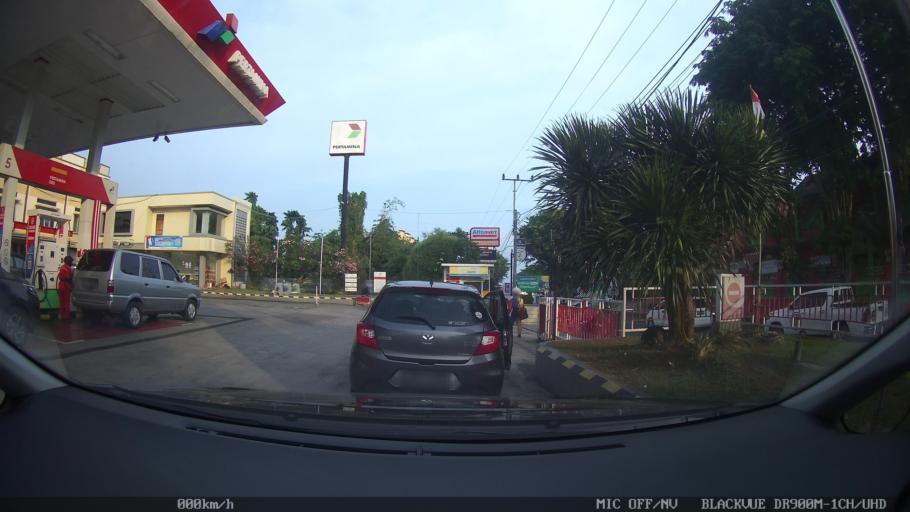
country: ID
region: Lampung
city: Bandarlampung
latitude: -5.4363
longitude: 105.2645
